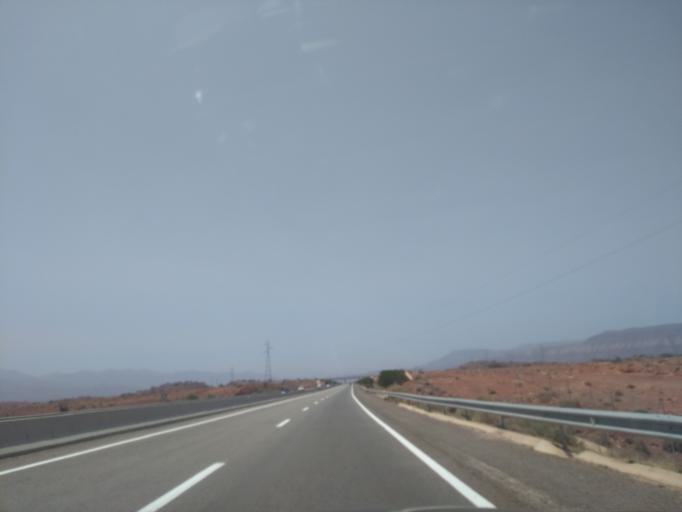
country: MA
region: Marrakech-Tensift-Al Haouz
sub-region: Chichaoua
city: Timezgadiouine
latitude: 30.8777
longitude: -9.0812
